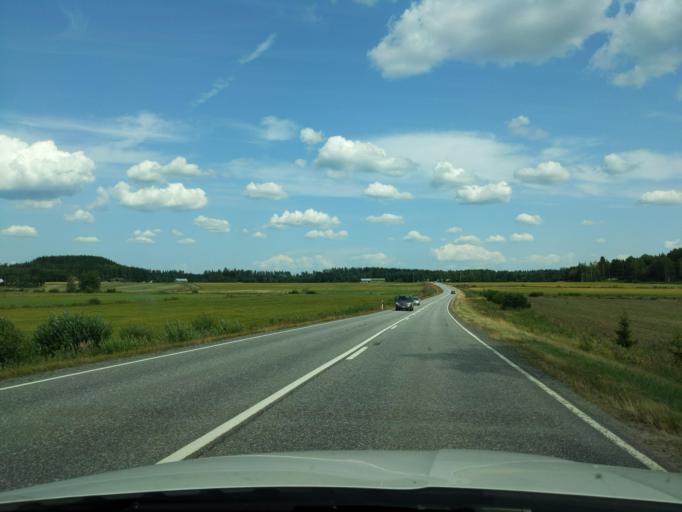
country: FI
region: Haeme
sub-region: Haemeenlinna
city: Lammi
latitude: 61.1225
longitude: 24.9455
